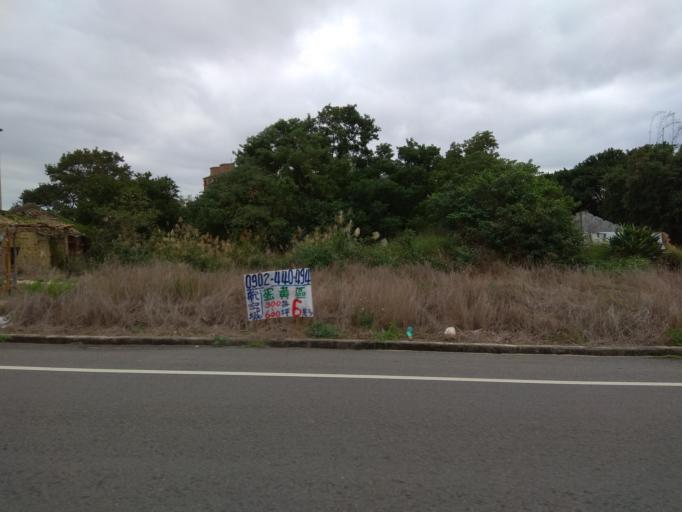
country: TW
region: Taiwan
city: Taoyuan City
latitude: 25.0469
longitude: 121.2231
